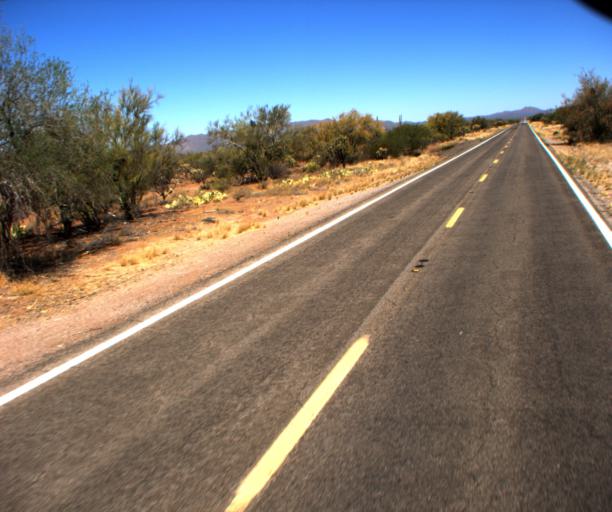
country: US
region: Arizona
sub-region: Pima County
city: Sells
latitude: 32.0480
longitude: -112.0236
